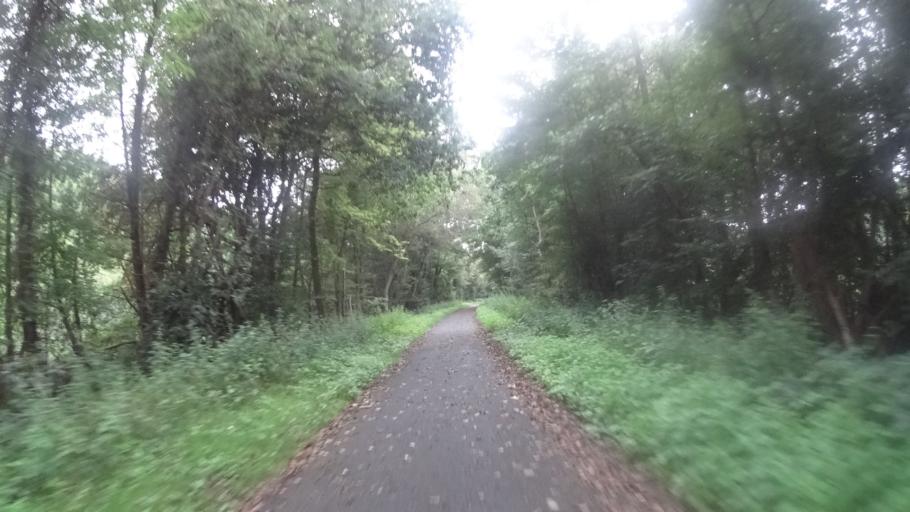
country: FR
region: Lorraine
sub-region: Departement de Meurthe-et-Moselle
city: Velaine-en-Haye
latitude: 48.6617
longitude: 6.0141
